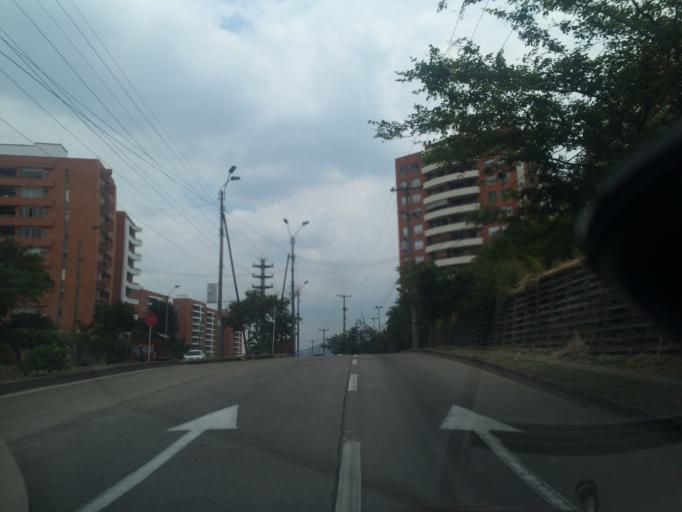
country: CO
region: Valle del Cauca
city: Cali
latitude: 3.4326
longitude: -76.5511
